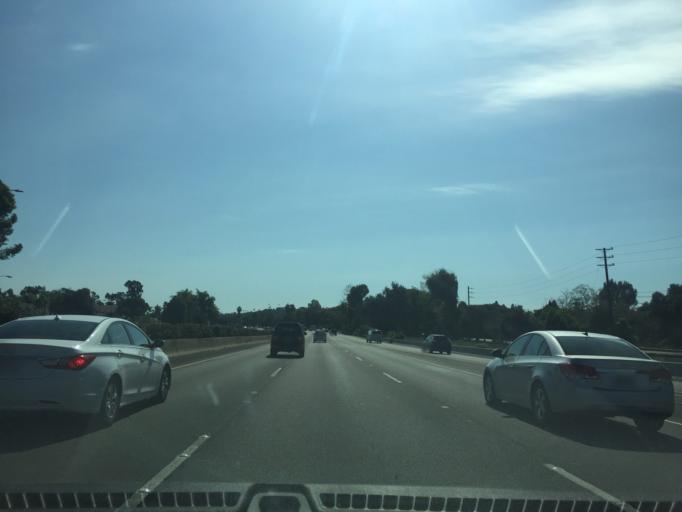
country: US
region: California
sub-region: Santa Barbara County
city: Mission Canyon
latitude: 34.4354
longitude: -119.7501
